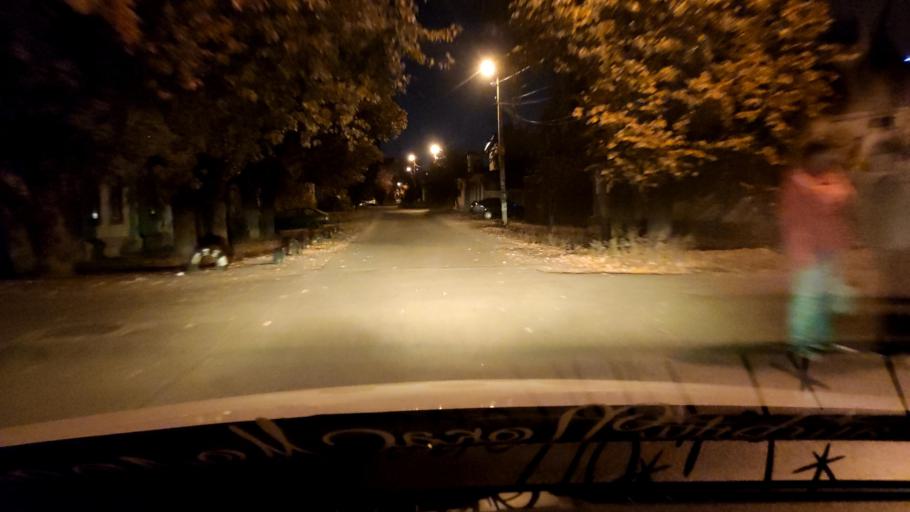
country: RU
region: Voronezj
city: Voronezh
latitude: 51.6458
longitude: 39.1781
